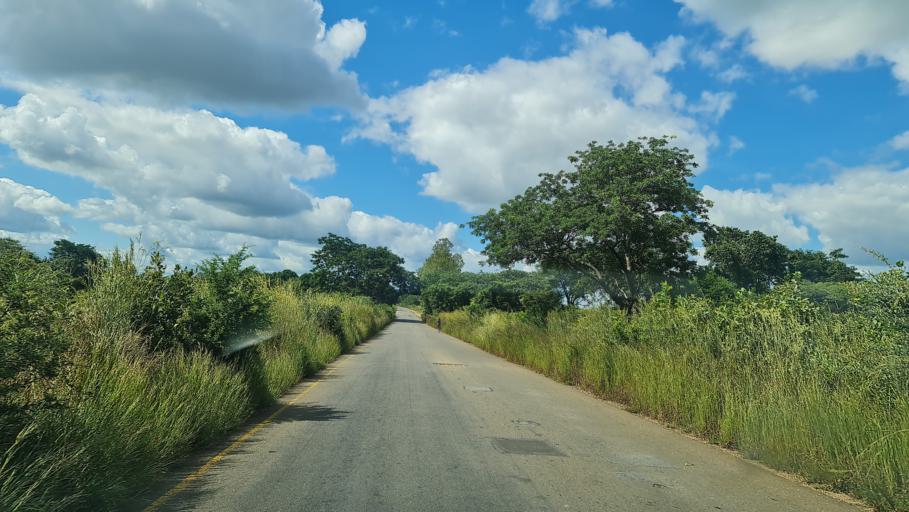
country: MZ
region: Zambezia
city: Quelimane
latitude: -17.5097
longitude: 36.2314
